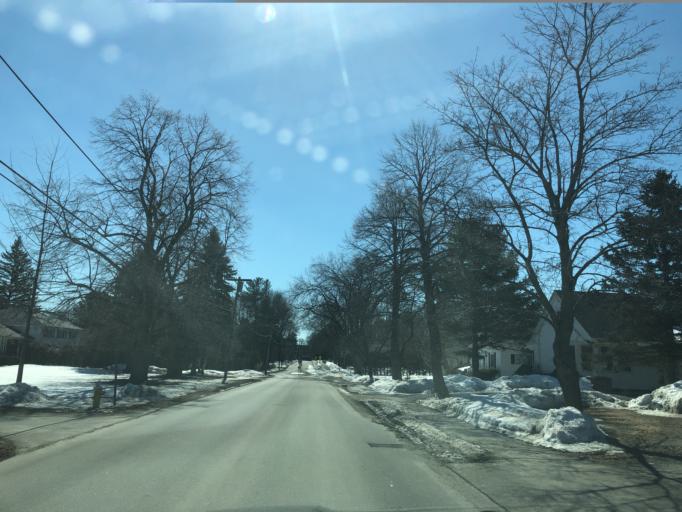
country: US
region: Maine
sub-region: Penobscot County
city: Brewer
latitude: 44.8153
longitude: -68.7536
